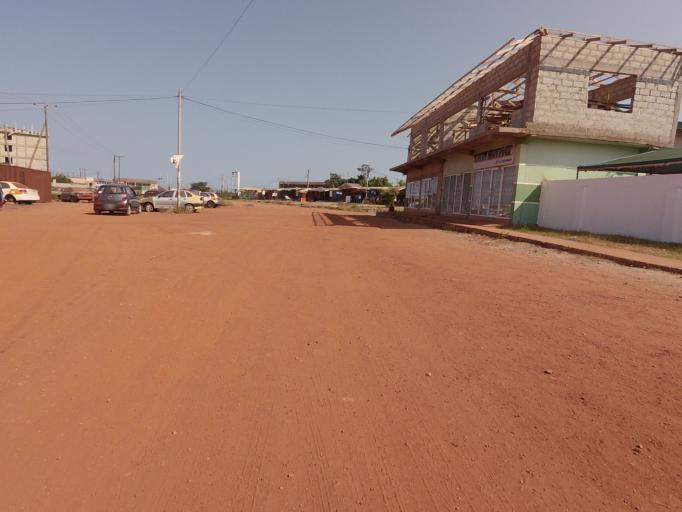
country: GH
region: Greater Accra
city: Teshi Old Town
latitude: 5.5780
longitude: -0.1121
